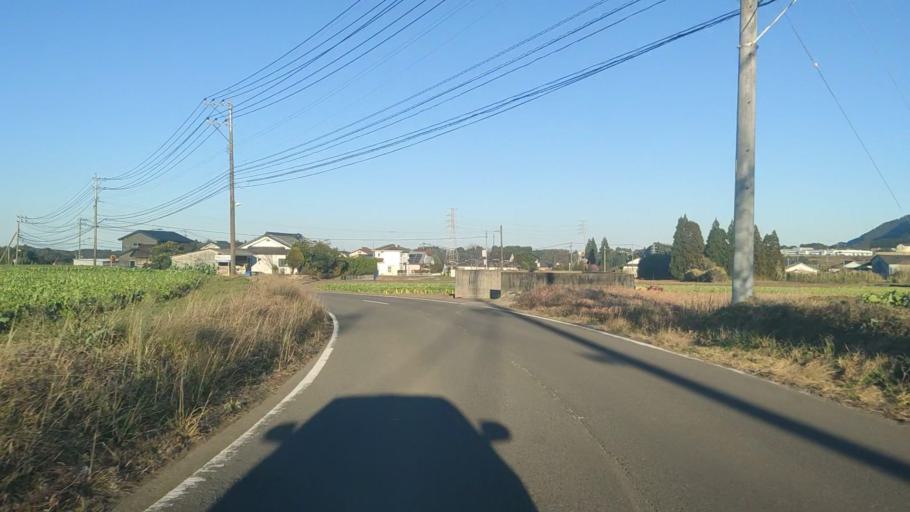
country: JP
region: Miyazaki
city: Miyazaki-shi
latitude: 31.8266
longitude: 131.3035
